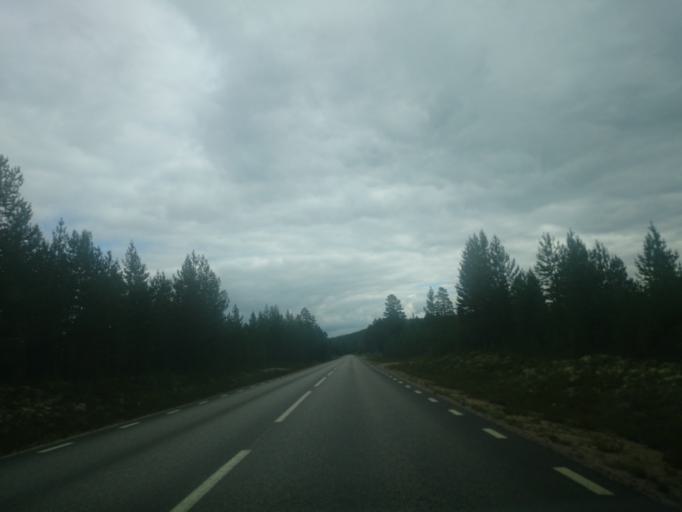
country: SE
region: Jaemtland
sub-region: Harjedalens Kommun
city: Sveg
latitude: 62.0321
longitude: 14.6674
